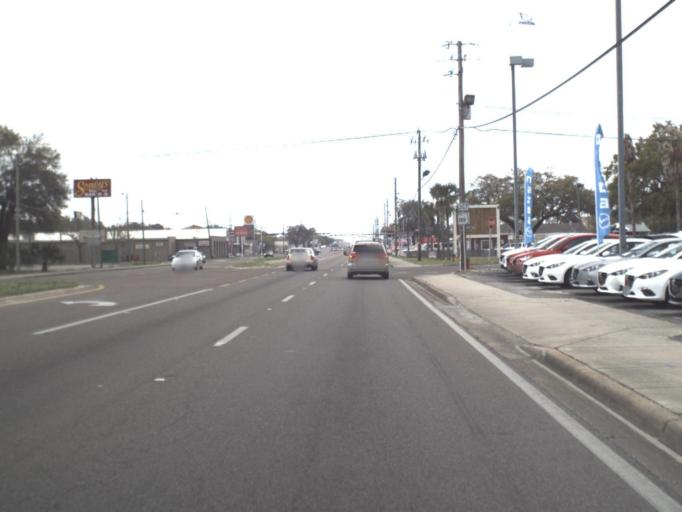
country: US
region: Florida
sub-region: Okaloosa County
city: Wright
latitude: 30.4524
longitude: -86.6386
